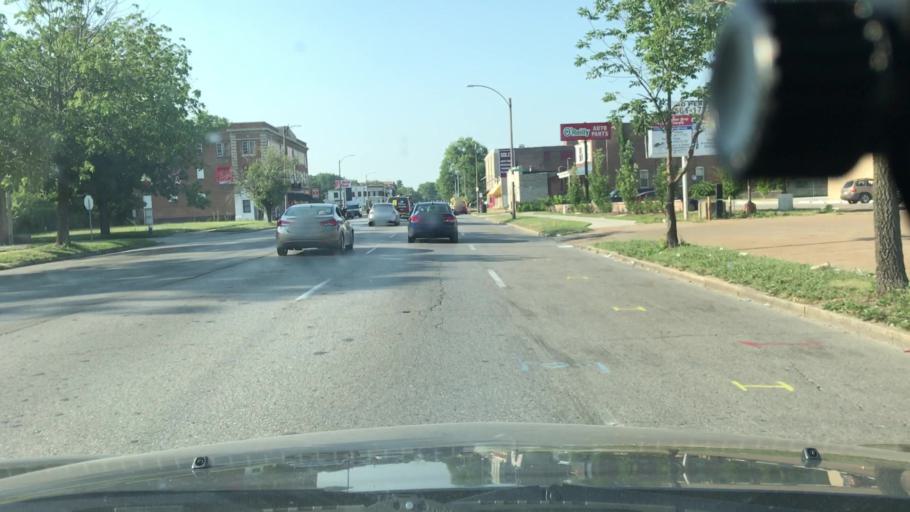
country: US
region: Missouri
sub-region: Saint Louis County
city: Hillsdale
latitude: 38.6566
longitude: -90.2626
